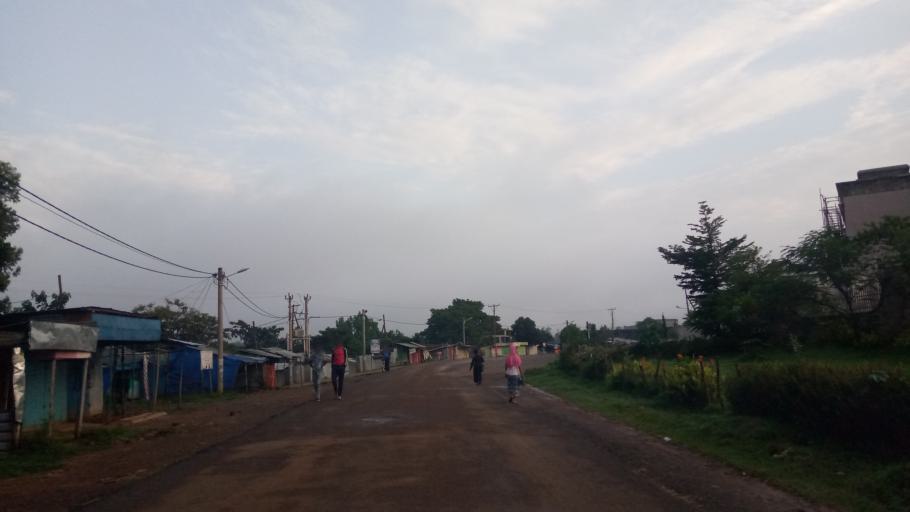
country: ET
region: Oromiya
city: Jima
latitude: 7.6779
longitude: 36.8511
